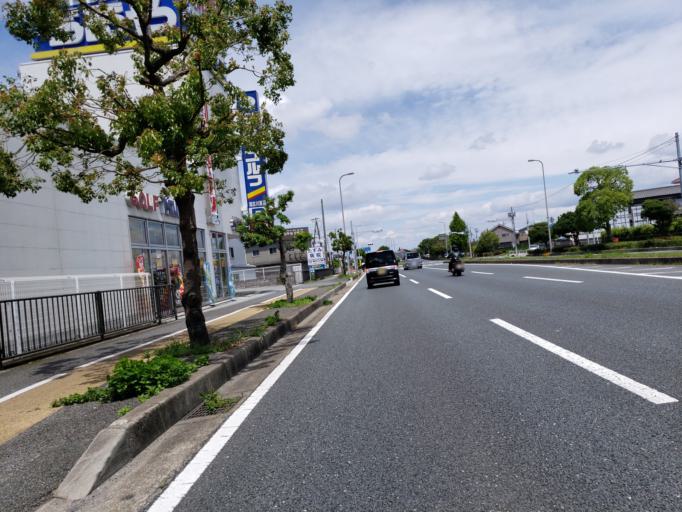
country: JP
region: Hyogo
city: Kakogawacho-honmachi
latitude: 34.7265
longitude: 134.8646
